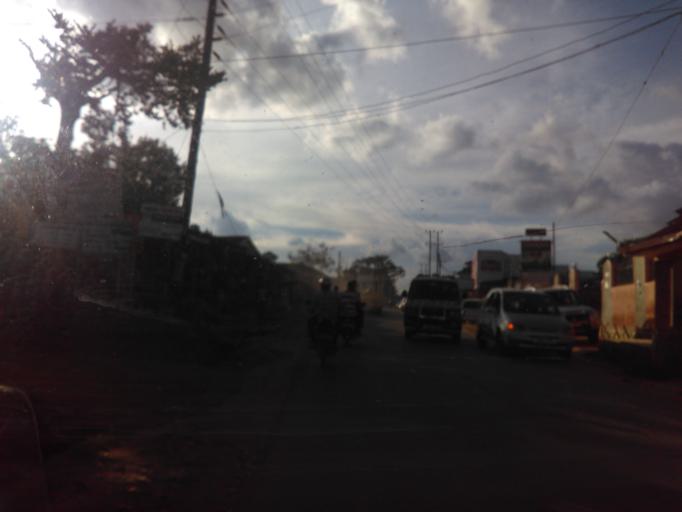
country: UG
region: Central Region
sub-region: Kampala District
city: Kampala
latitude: 0.2702
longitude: 32.5568
